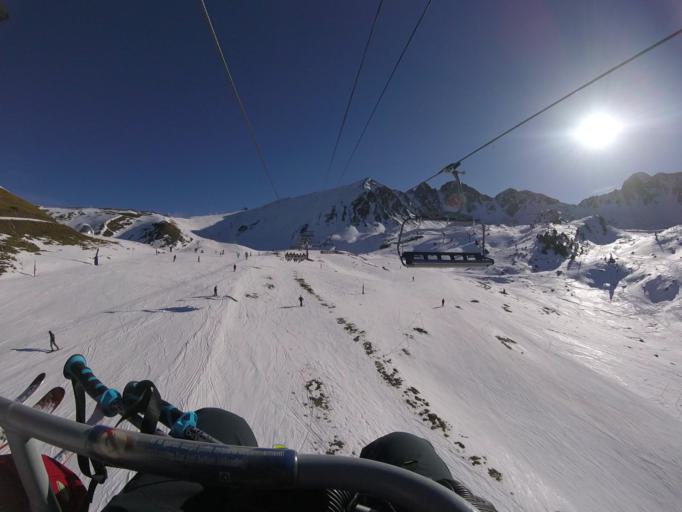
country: AD
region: Encamp
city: Pas de la Casa
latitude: 42.5268
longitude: 1.7100
